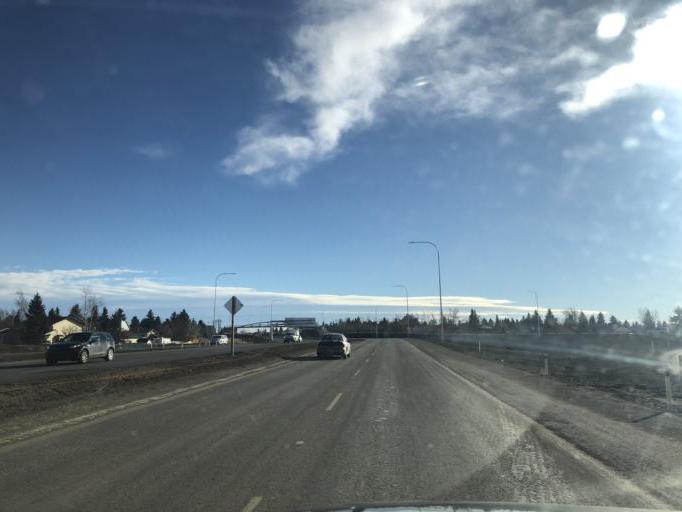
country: CA
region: Alberta
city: Calgary
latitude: 50.9512
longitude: -114.1378
